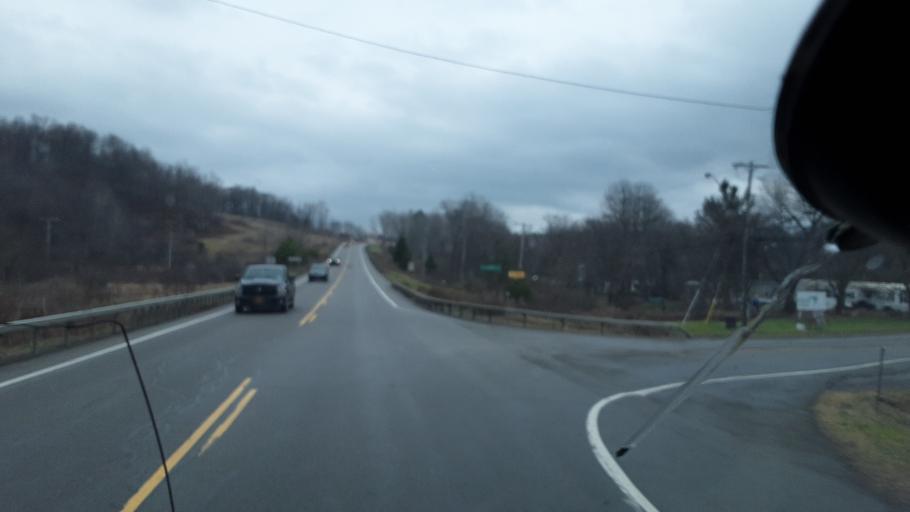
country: US
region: New York
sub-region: Allegany County
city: Houghton
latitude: 42.3876
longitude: -78.2310
